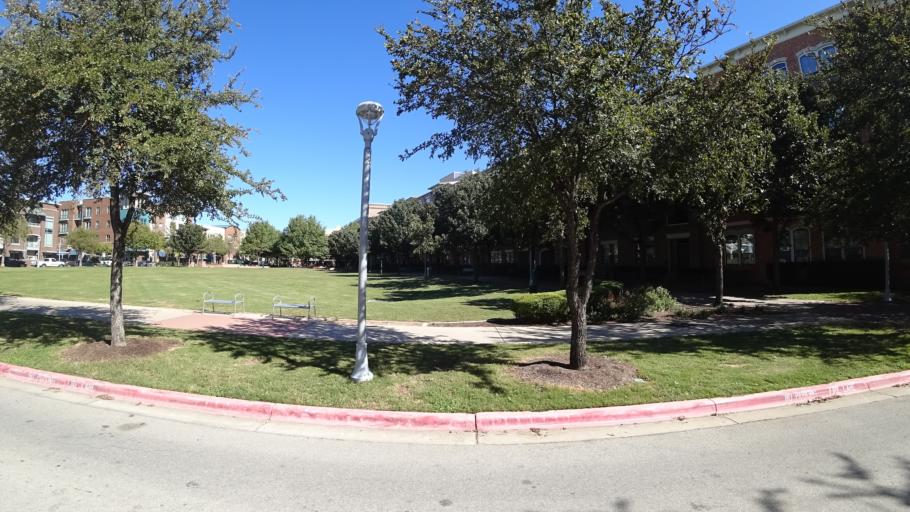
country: US
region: Texas
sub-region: Travis County
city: Austin
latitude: 30.3137
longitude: -97.7336
